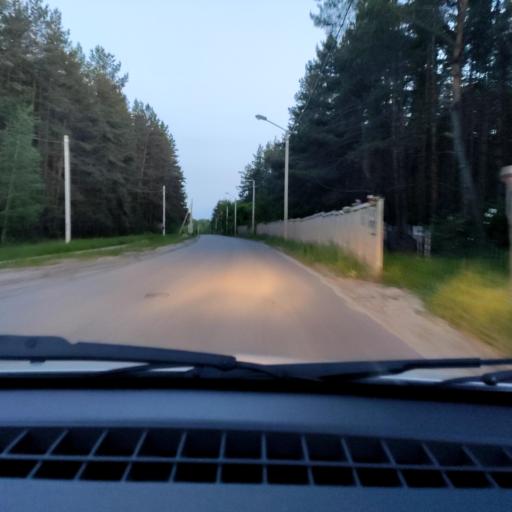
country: RU
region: Voronezj
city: Pridonskoy
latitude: 51.6951
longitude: 39.1044
